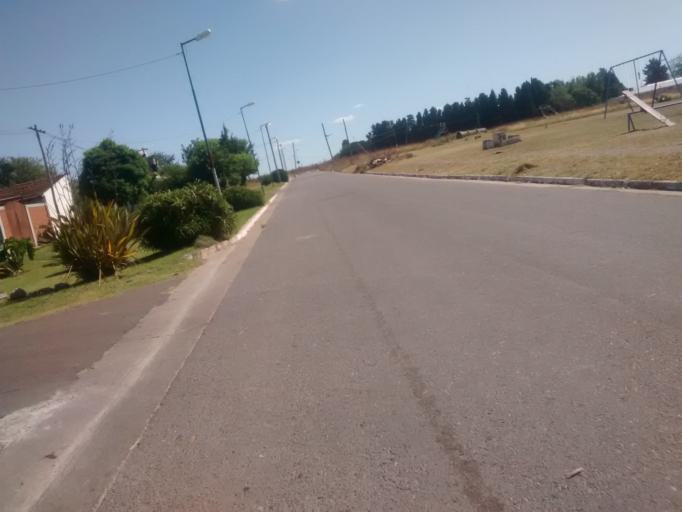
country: AR
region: Buenos Aires
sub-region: Partido de La Plata
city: La Plata
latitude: -34.9349
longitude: -57.9041
